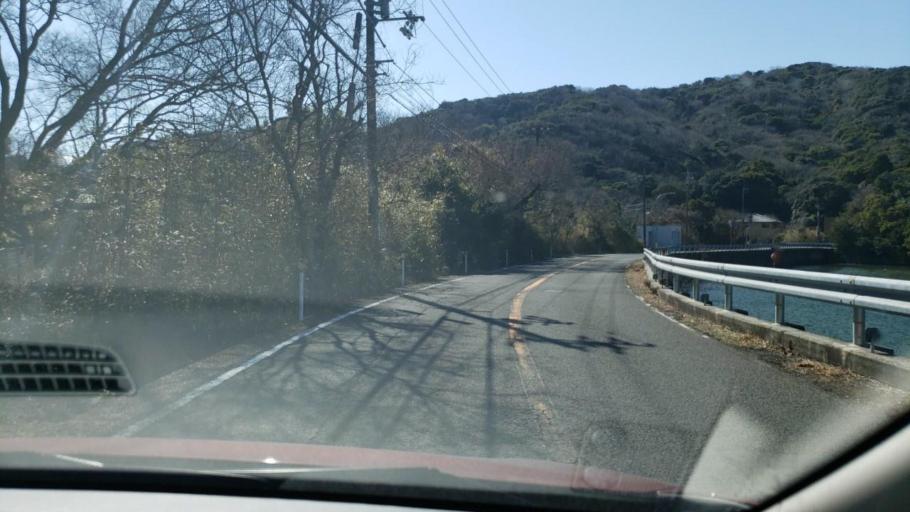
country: JP
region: Tokushima
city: Narutocho-mitsuishi
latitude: 34.2213
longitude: 134.5754
